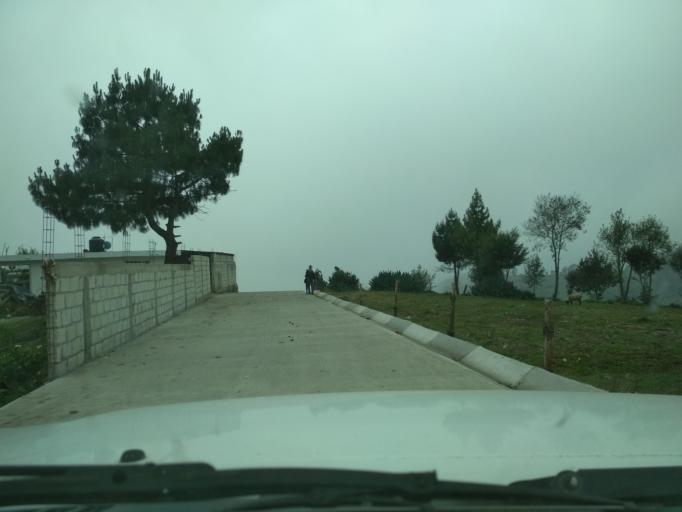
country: MX
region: Veracruz
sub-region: Mariano Escobedo
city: San Isidro el Berro
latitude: 18.9745
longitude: -97.2050
